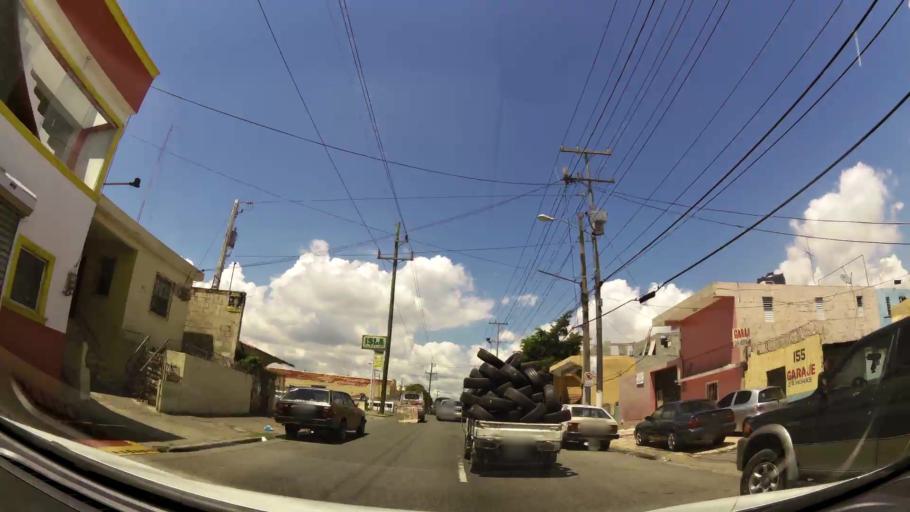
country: DO
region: Nacional
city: Ensanche Luperon
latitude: 18.4933
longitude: -69.8927
